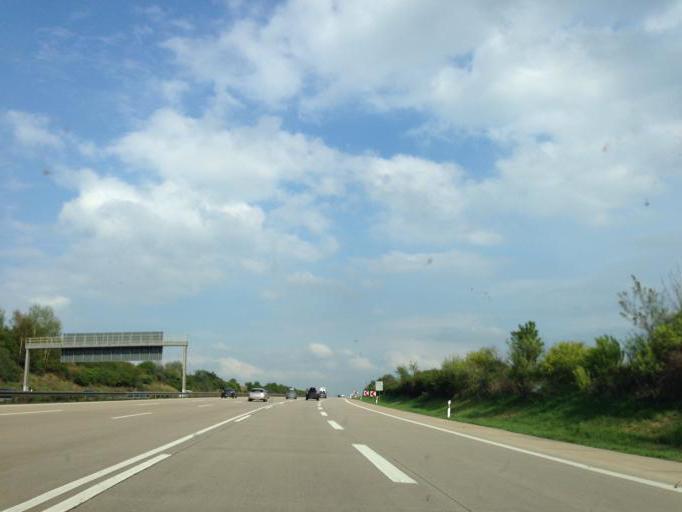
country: DE
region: Saxony
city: Reinsberg
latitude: 51.0588
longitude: 13.3836
